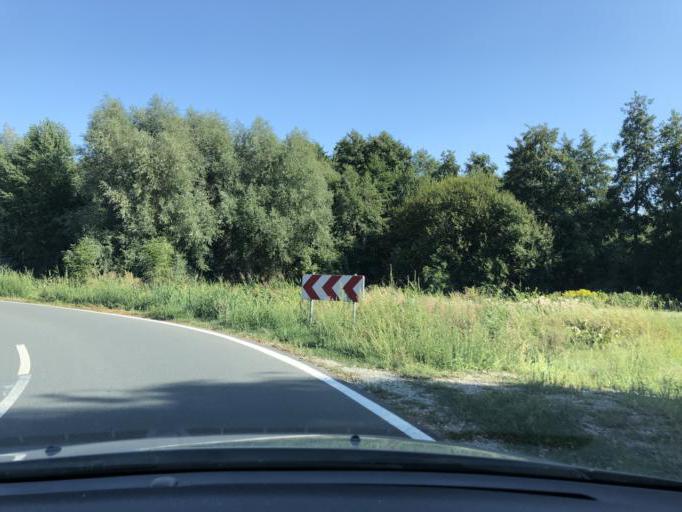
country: DE
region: Thuringia
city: Rastenberg
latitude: 51.1964
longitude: 11.4771
